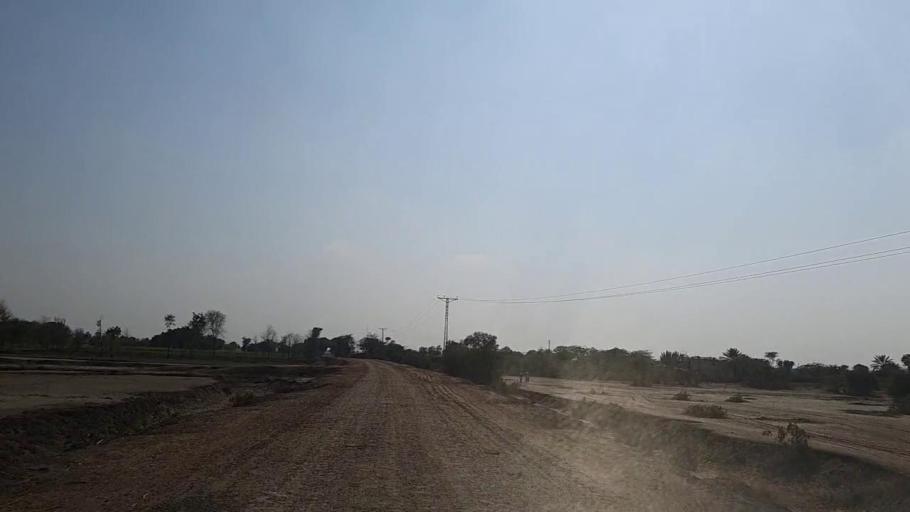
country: PK
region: Sindh
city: Daur
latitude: 26.4531
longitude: 68.2347
